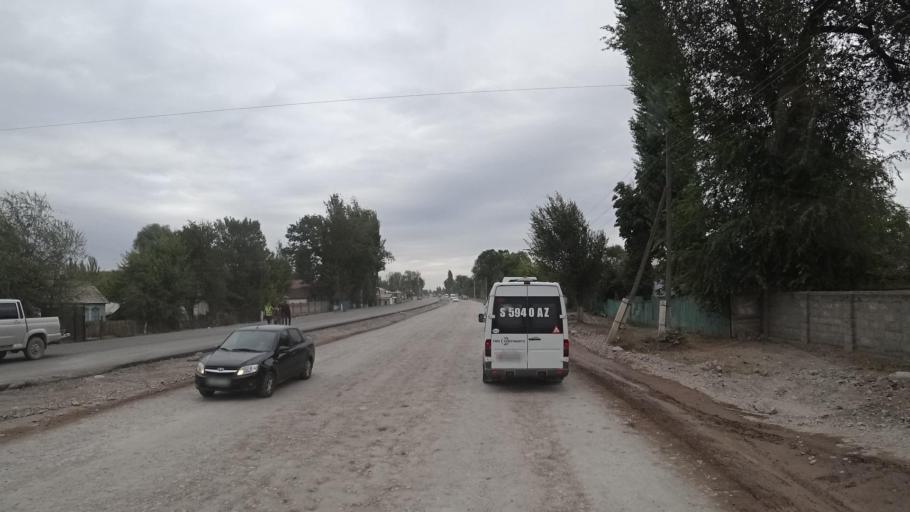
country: KG
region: Chuy
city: Belovodskoye
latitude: 42.8402
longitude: 74.1448
